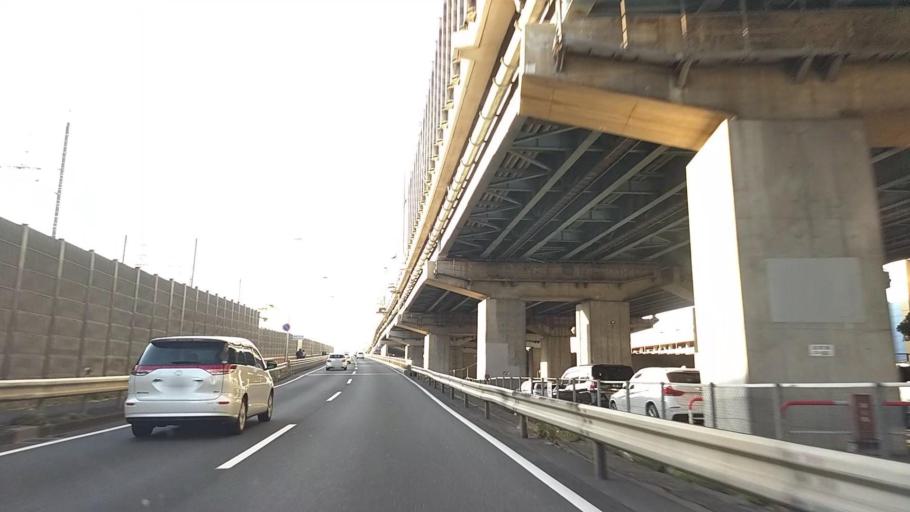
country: JP
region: Chiba
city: Funabashi
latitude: 35.6848
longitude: 139.9898
